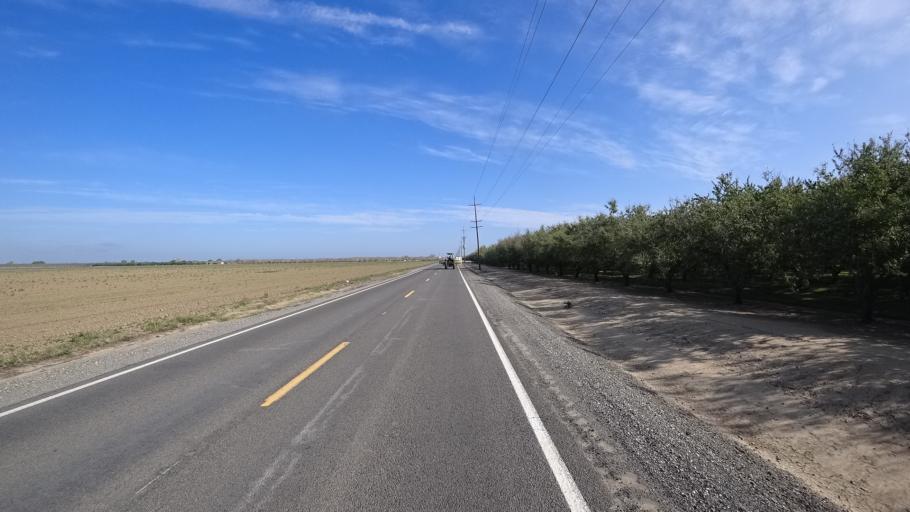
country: US
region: California
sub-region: Glenn County
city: Hamilton City
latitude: 39.6099
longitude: -122.0075
